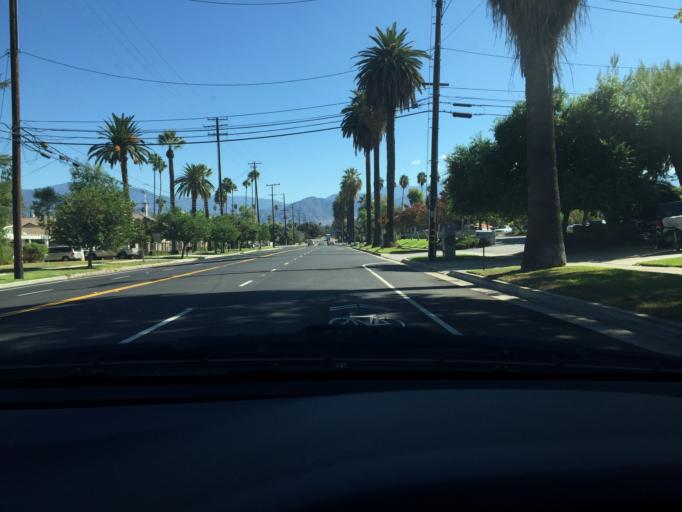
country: US
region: California
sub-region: San Bernardino County
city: Redlands
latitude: 34.0491
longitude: -117.1732
